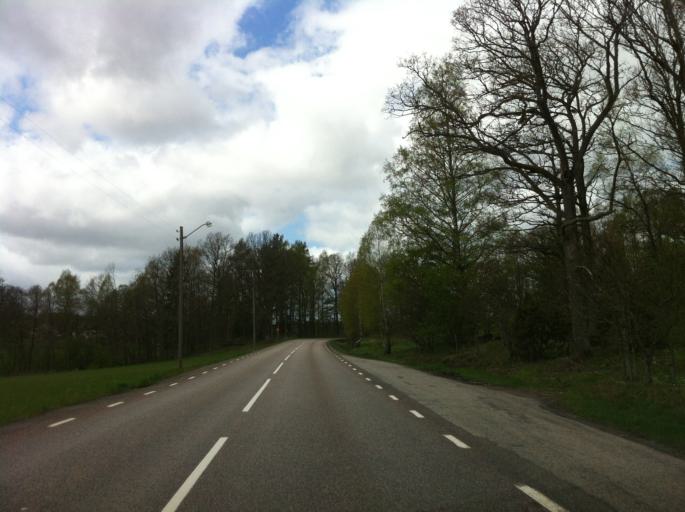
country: SE
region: Vaestra Goetaland
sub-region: Alingsas Kommun
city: Ingared
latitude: 57.8428
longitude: 12.4925
